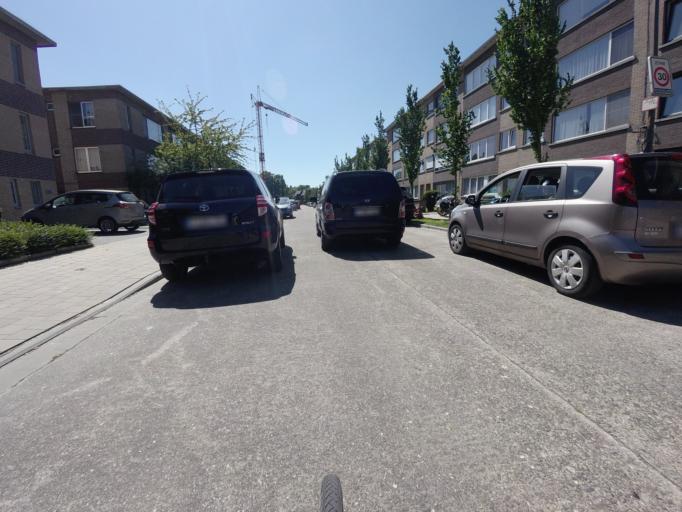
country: BE
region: Flanders
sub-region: Provincie Antwerpen
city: Hove
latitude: 51.1729
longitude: 4.4765
